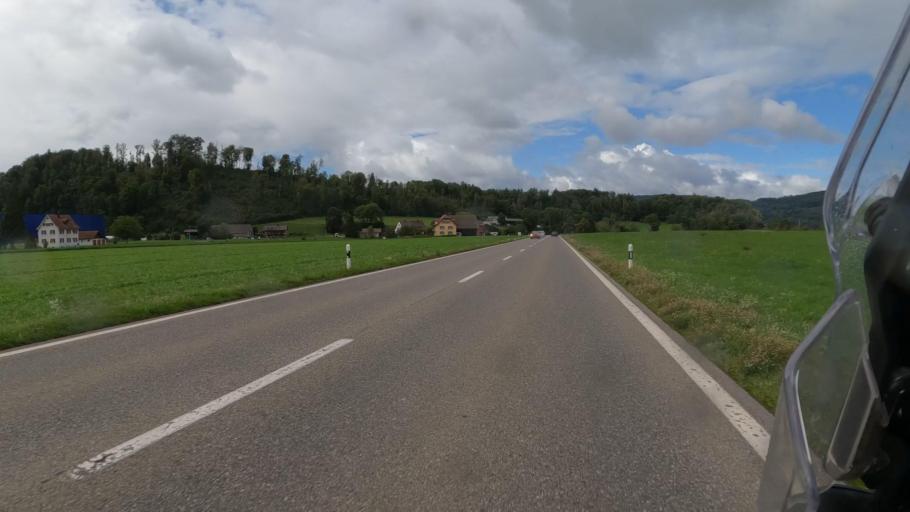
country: DE
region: Baden-Wuerttemberg
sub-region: Freiburg Region
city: Hohentengen am Hochrhein
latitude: 47.5683
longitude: 8.4113
